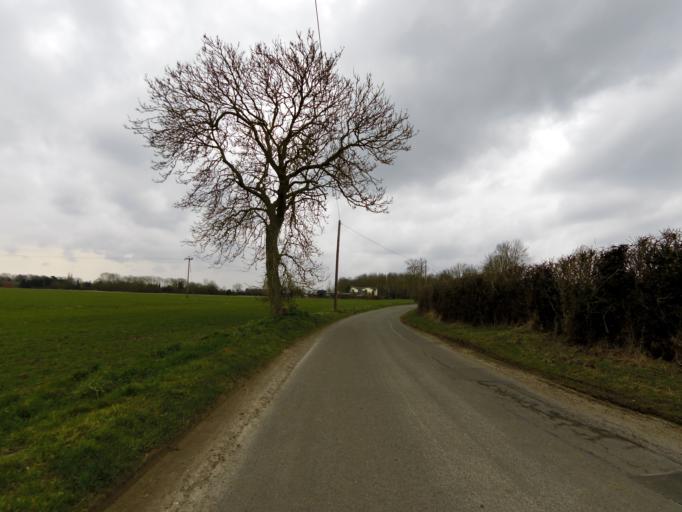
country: GB
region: England
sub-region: Suffolk
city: Halesworth
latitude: 52.3891
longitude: 1.5194
